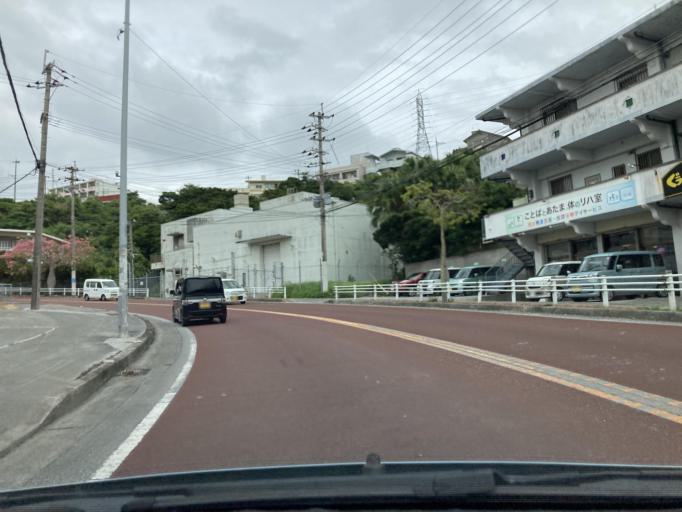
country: JP
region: Okinawa
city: Ginowan
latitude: 26.2363
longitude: 127.7540
